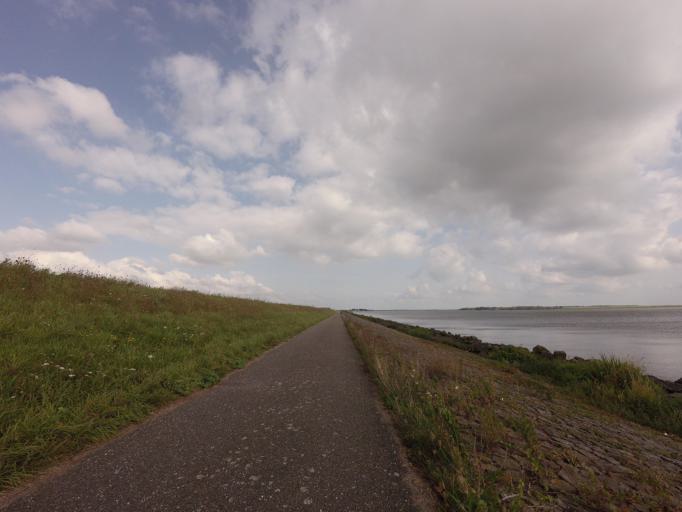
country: NL
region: Flevoland
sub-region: Gemeente Dronten
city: Dronten
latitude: 52.6130
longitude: 5.7149
